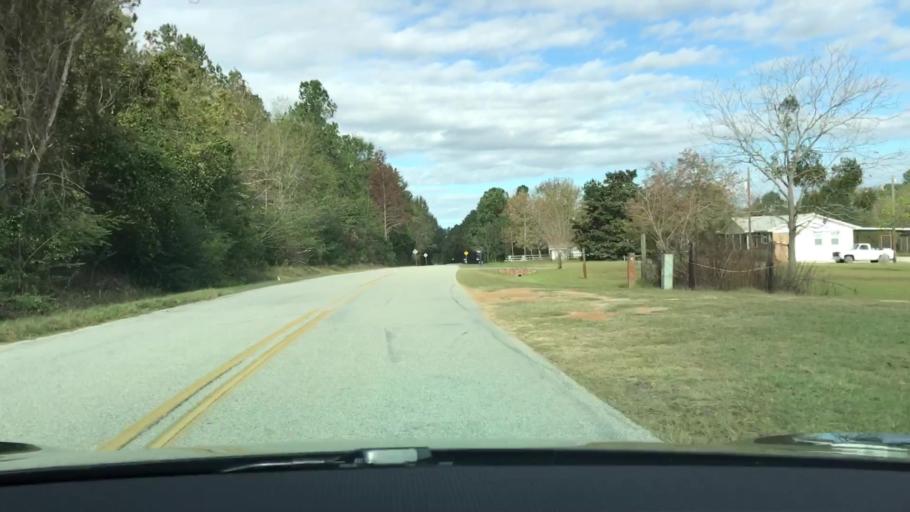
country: US
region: Georgia
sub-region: Jefferson County
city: Wadley
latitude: 32.8019
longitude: -82.3857
